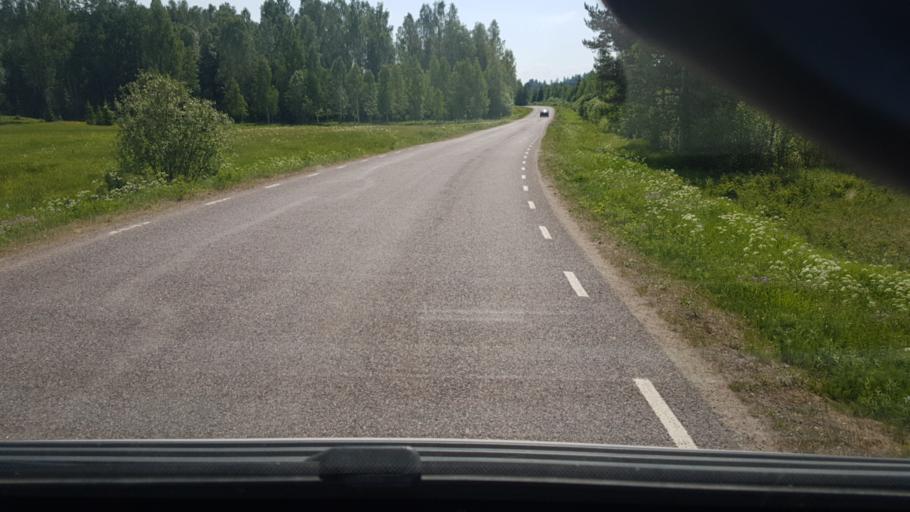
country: SE
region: Vaermland
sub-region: Eda Kommun
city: Charlottenberg
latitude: 59.9726
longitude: 12.4114
